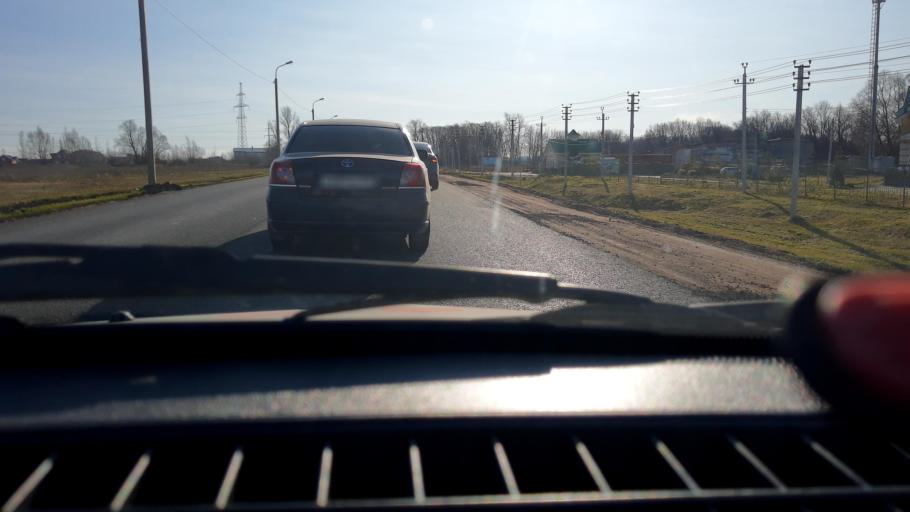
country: RU
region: Bashkortostan
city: Kabakovo
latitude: 54.6362
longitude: 56.0939
